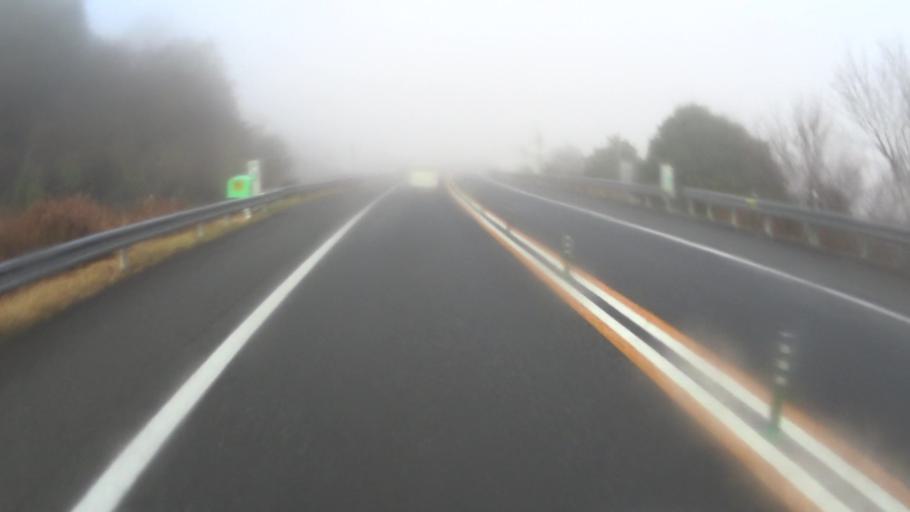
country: JP
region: Kyoto
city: Kameoka
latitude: 35.1279
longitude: 135.4620
